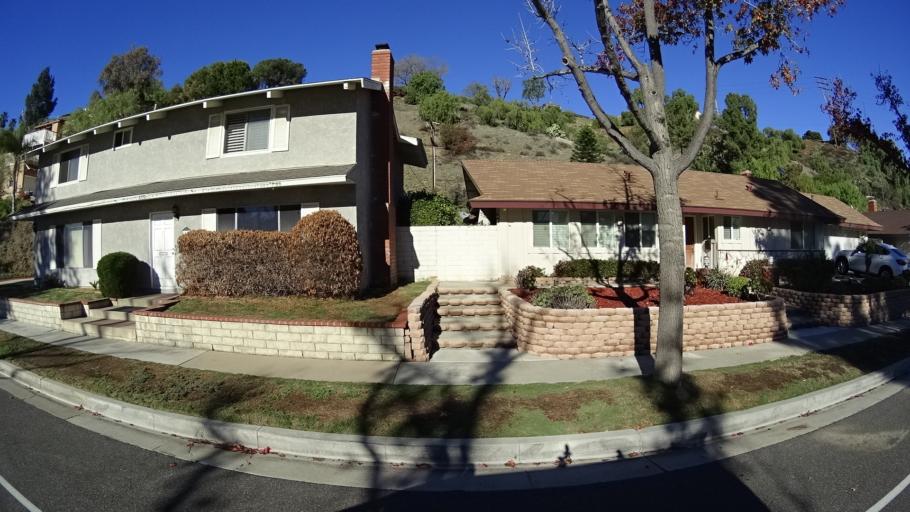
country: US
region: California
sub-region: Orange County
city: Yorba Linda
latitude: 33.8672
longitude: -117.7879
